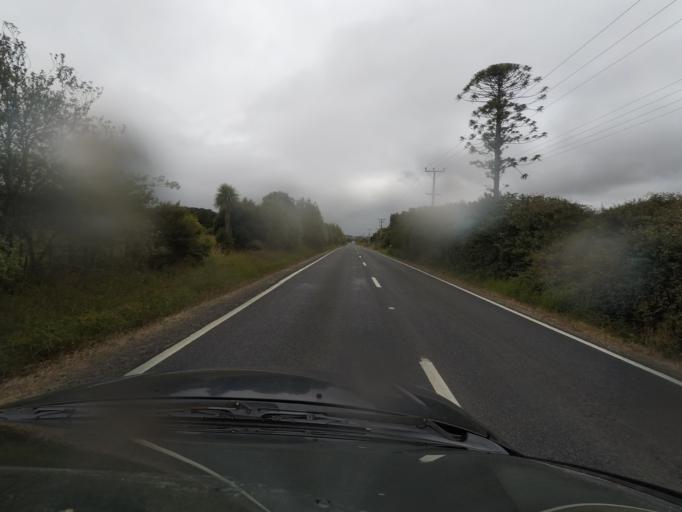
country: NZ
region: Auckland
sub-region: Auckland
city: Warkworth
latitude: -36.3439
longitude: 174.7072
